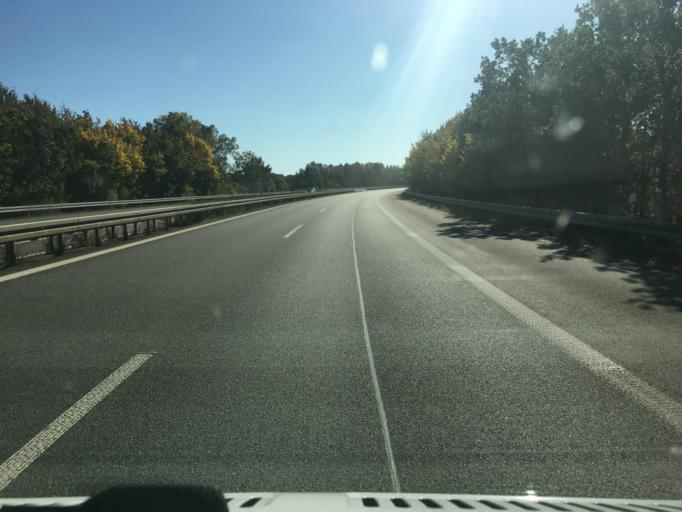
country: DE
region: Saxony
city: Dennheritz
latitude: 50.7815
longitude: 12.4927
